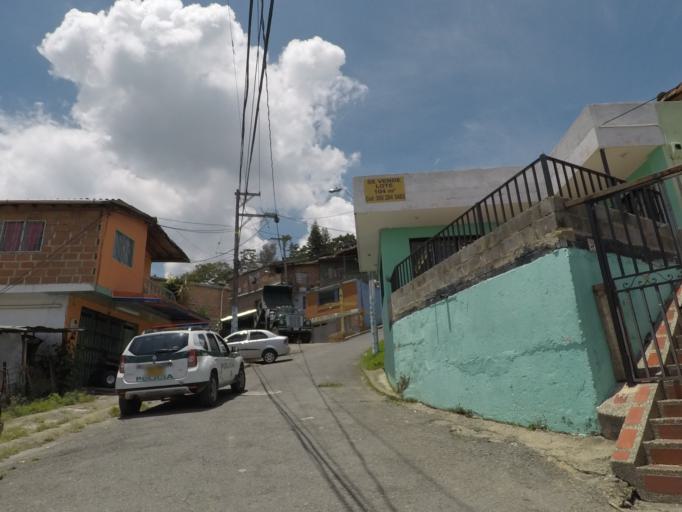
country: CO
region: Antioquia
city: Medellin
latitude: 6.2709
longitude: -75.6349
